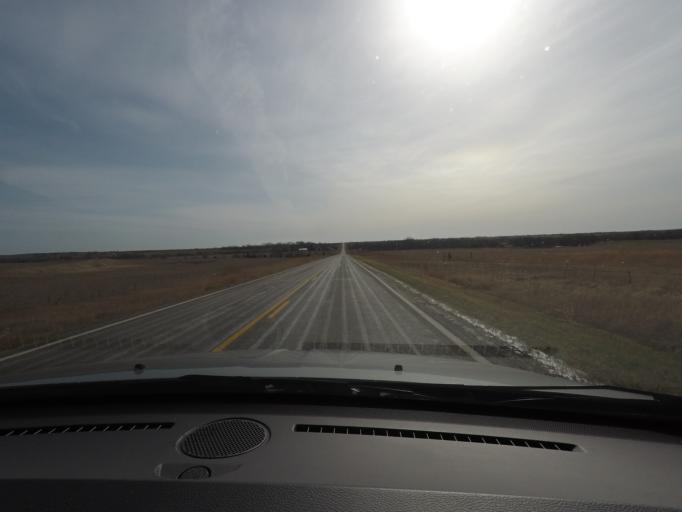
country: US
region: Kansas
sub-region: Morris County
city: Council Grove
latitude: 38.6589
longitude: -96.2346
